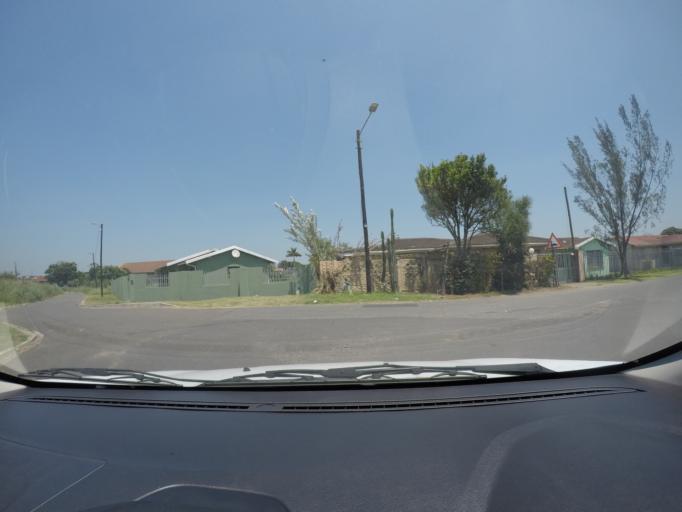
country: ZA
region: KwaZulu-Natal
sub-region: uThungulu District Municipality
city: eSikhawini
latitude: -28.8724
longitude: 31.9065
